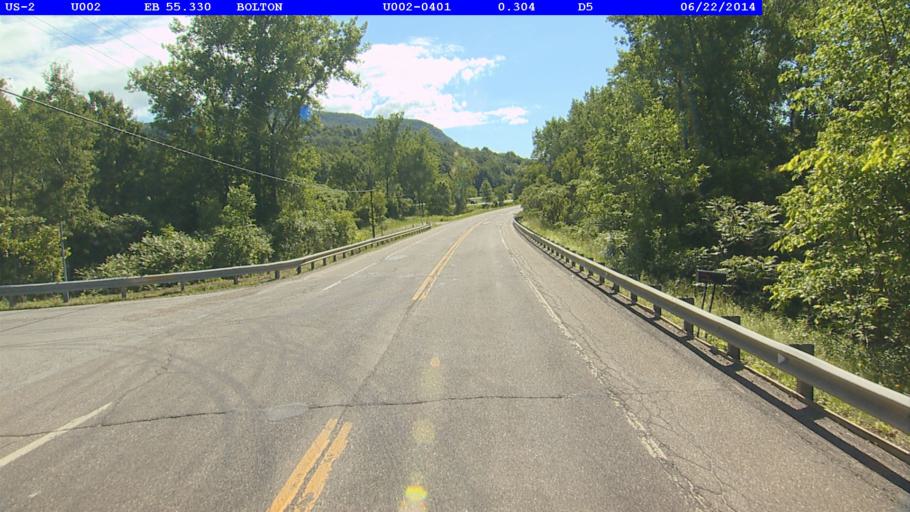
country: US
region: Vermont
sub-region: Chittenden County
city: Jericho
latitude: 44.3824
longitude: -72.9275
